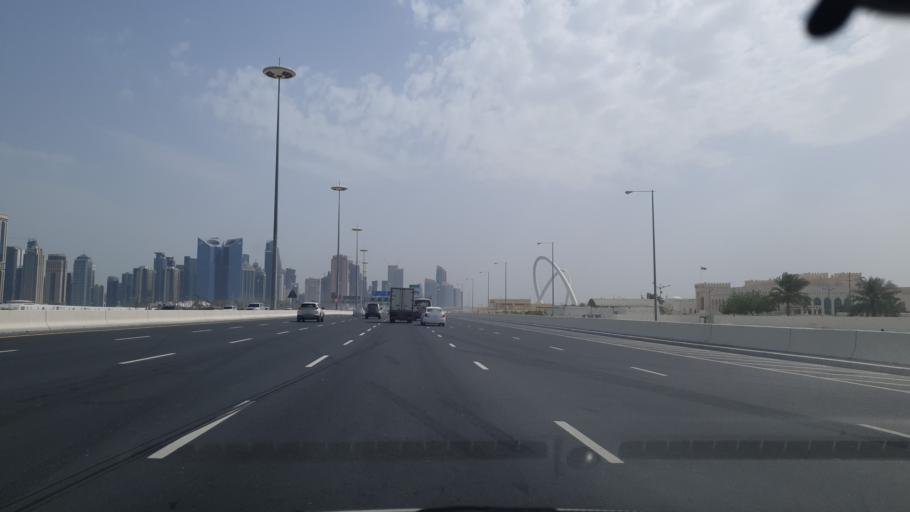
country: QA
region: Baladiyat ad Dawhah
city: Doha
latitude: 25.3457
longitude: 51.5203
